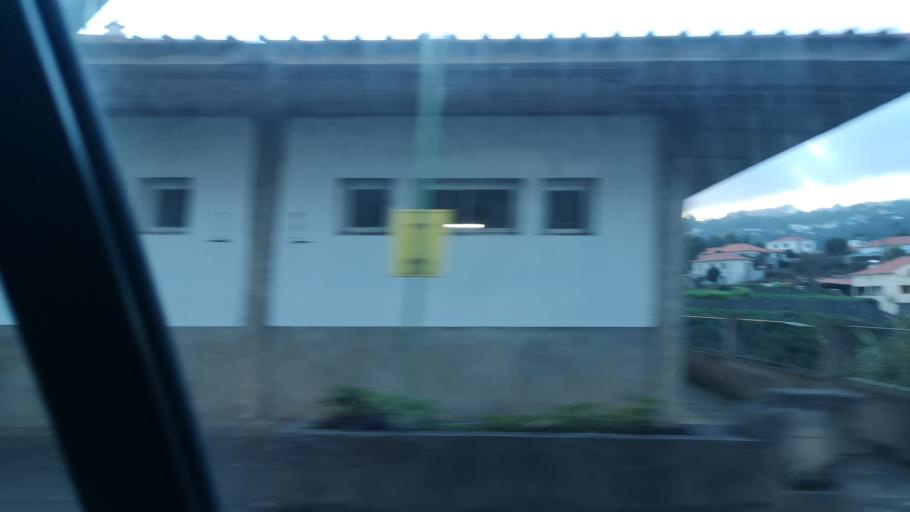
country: PT
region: Madeira
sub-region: Santa Cruz
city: Camacha
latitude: 32.6762
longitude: -16.8248
